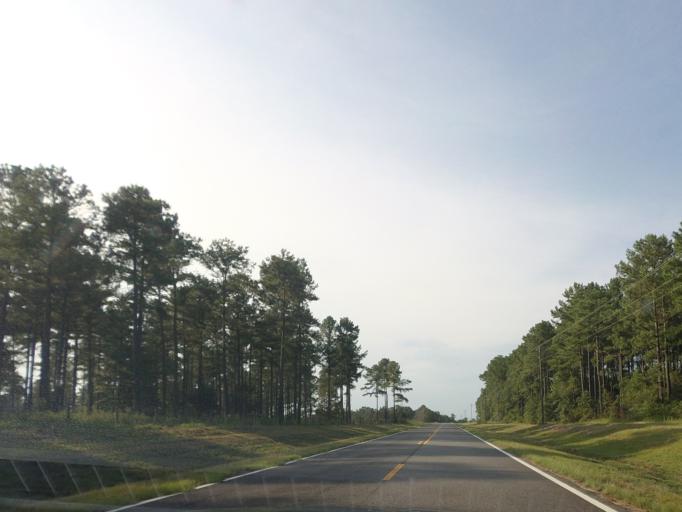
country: US
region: Georgia
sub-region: Bleckley County
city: Cochran
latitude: 32.4754
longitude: -83.3013
